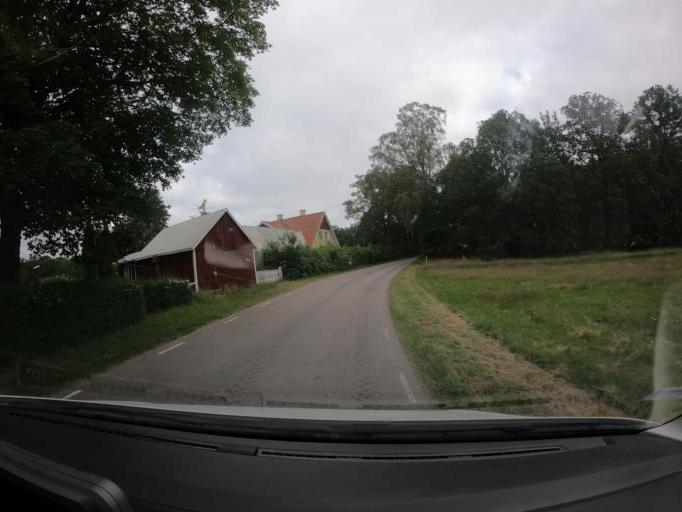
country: SE
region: Skane
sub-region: Klippans Kommun
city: Ljungbyhed
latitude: 56.0487
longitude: 13.2550
